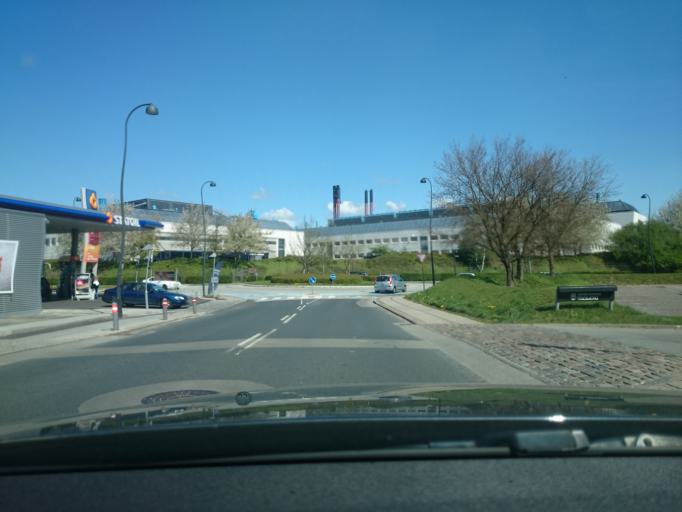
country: DK
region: Capital Region
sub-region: Lyngby-Tarbaek Kommune
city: Kongens Lyngby
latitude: 55.7546
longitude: 12.5132
